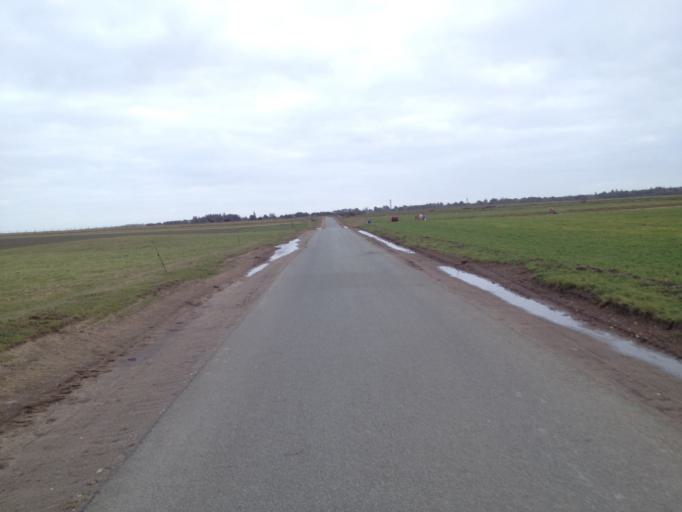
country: DE
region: Schleswig-Holstein
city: Nebel
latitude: 54.6632
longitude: 8.3468
